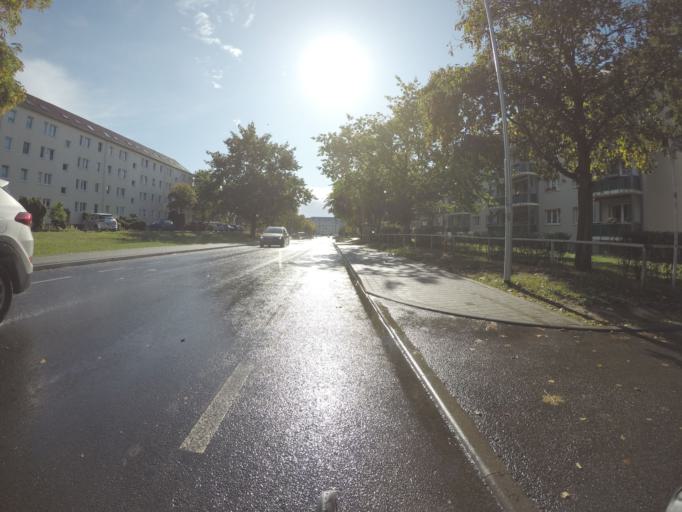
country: DE
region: Brandenburg
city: Strausberg
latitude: 52.5801
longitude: 13.8893
